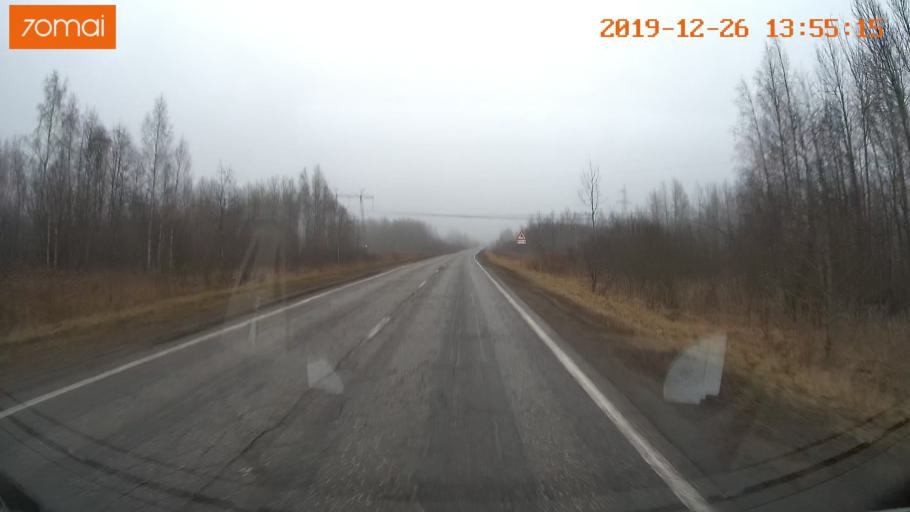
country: RU
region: Jaroslavl
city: Poshekhon'ye
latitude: 58.6056
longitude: 38.6449
